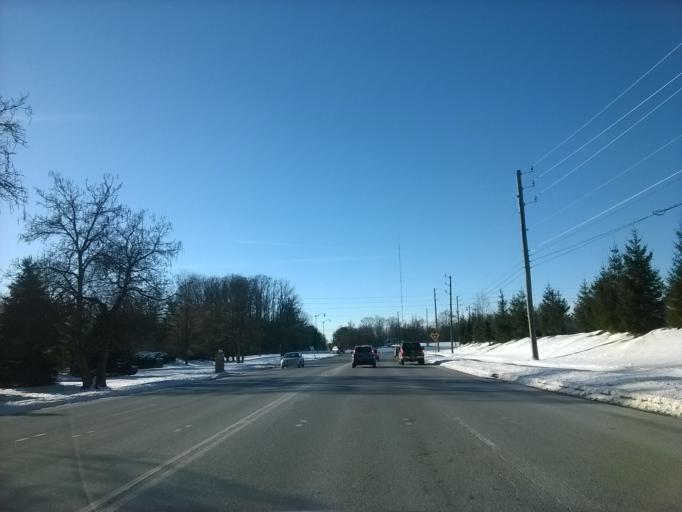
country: US
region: Indiana
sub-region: Marion County
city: Meridian Hills
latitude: 39.9270
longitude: -86.1632
